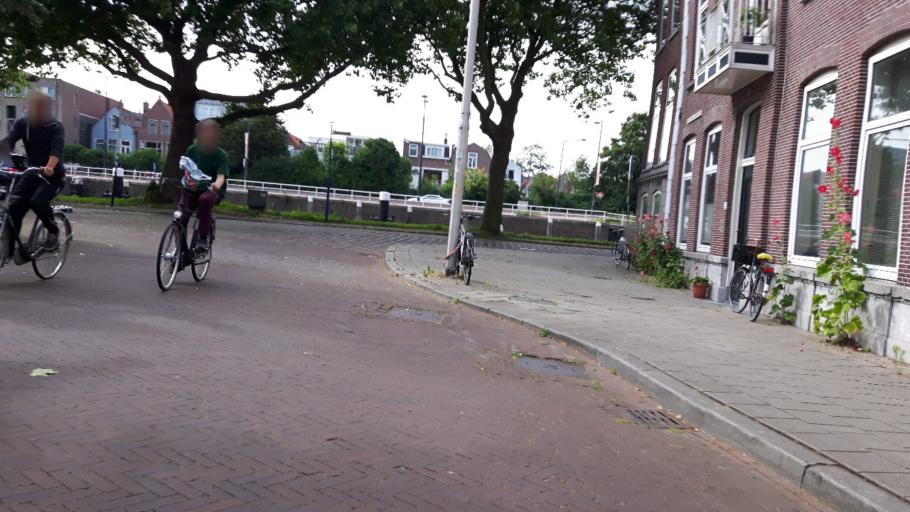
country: NL
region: South Holland
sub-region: Gemeente Delft
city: Delft
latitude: 52.0059
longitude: 4.3629
